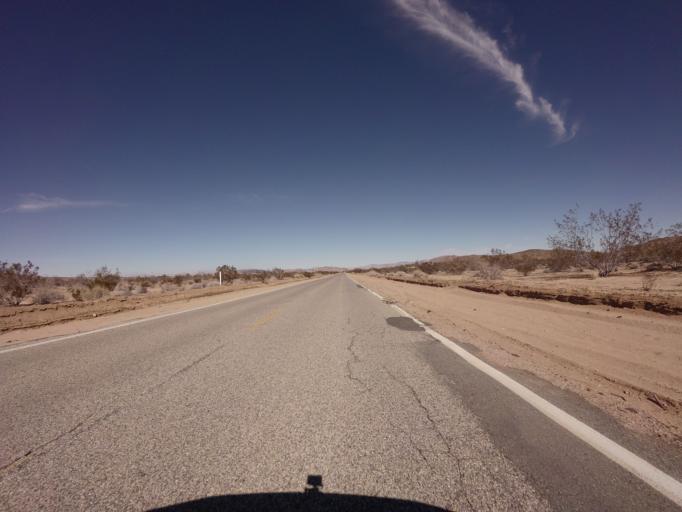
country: US
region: California
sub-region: San Bernardino County
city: Joshua Tree
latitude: 34.2474
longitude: -116.3932
